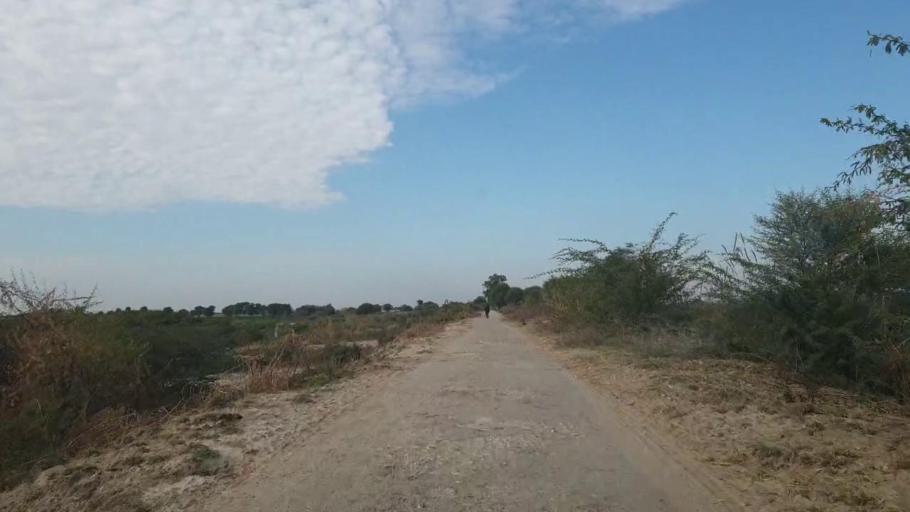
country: PK
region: Sindh
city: Sinjhoro
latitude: 26.0369
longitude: 68.8781
